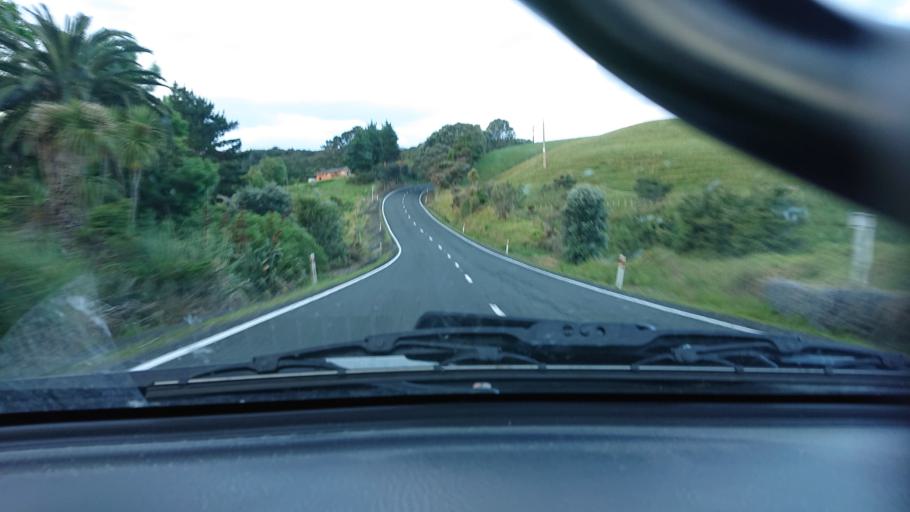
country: NZ
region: Auckland
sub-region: Auckland
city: Wellsford
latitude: -36.4394
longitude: 174.4320
